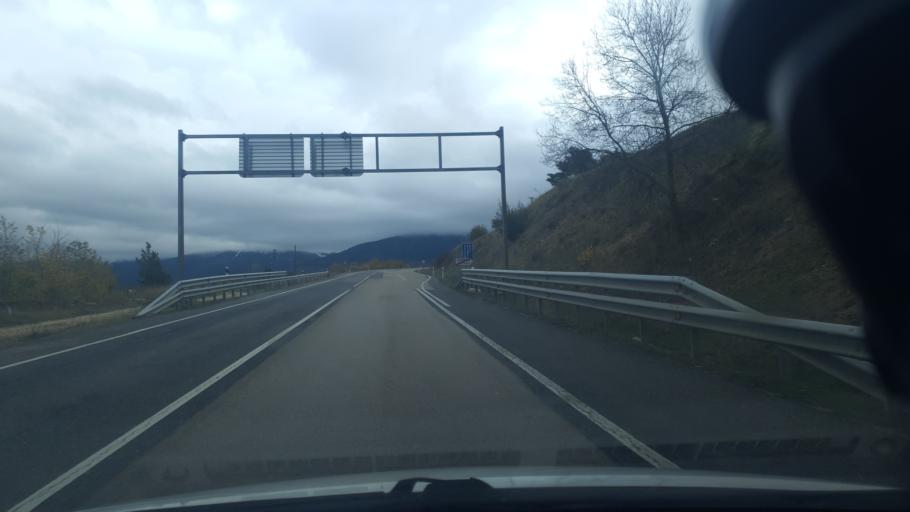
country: ES
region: Castille and Leon
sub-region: Provincia de Segovia
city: Cerezo de Abajo
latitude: 41.2161
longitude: -3.5890
